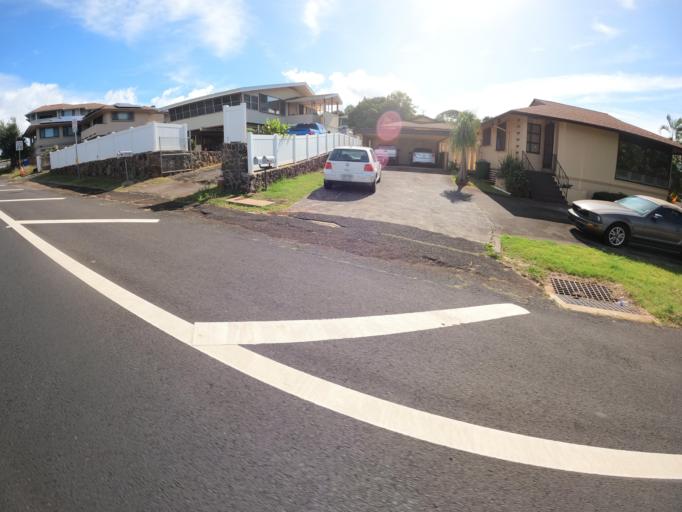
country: US
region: Hawaii
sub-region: Honolulu County
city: Halawa Heights
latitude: 21.3838
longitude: -157.9151
